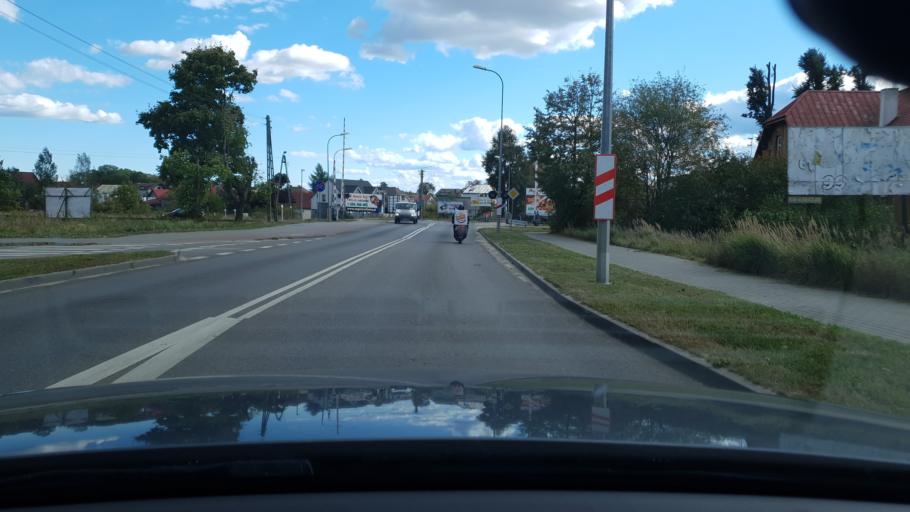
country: PL
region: Pomeranian Voivodeship
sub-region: Powiat wejherowski
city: Reda
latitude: 54.6156
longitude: 18.3459
